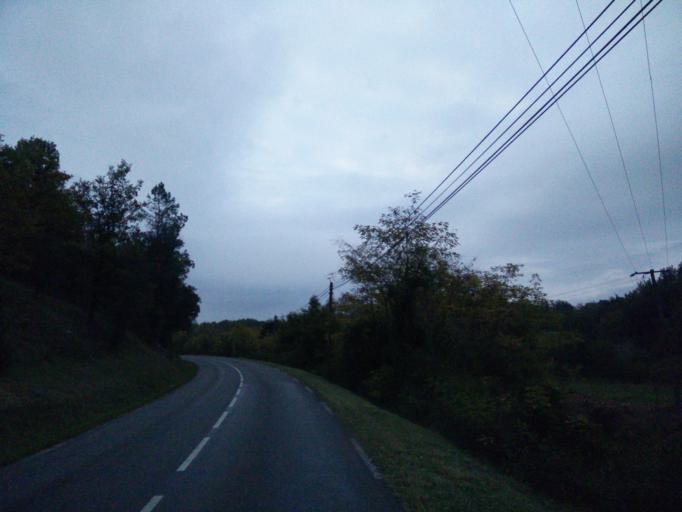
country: FR
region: Aquitaine
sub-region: Departement de la Dordogne
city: Carsac-Aillac
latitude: 44.7856
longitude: 1.3131
